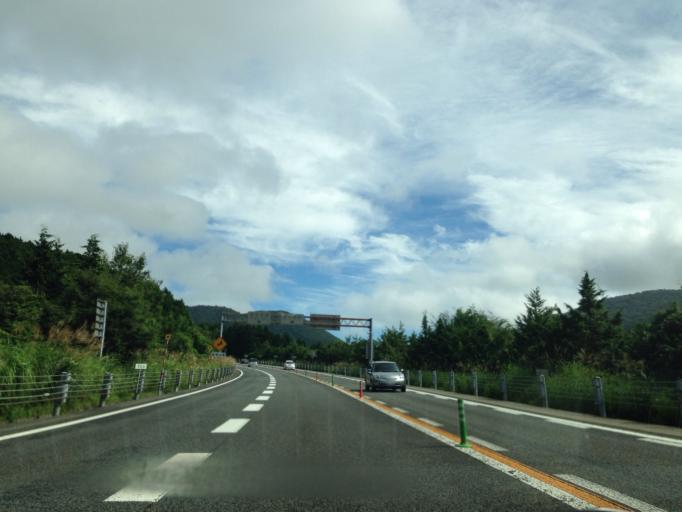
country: JP
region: Shizuoka
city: Gotemba
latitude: 35.3687
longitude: 138.8489
